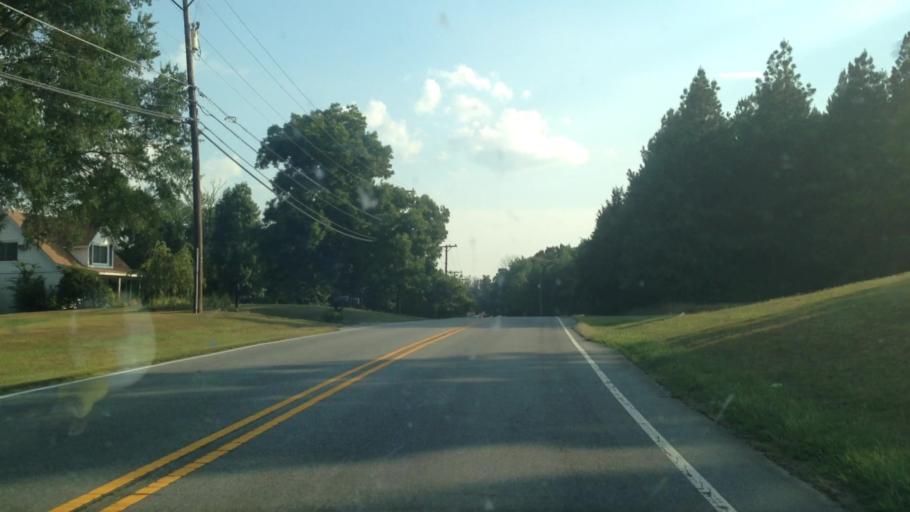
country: US
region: North Carolina
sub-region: Guilford County
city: High Point
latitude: 35.9914
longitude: -80.0629
